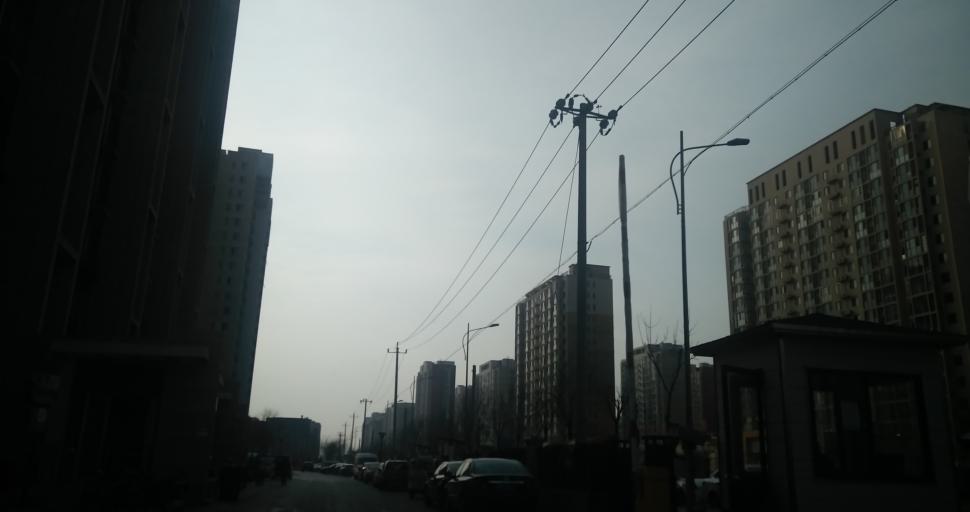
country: CN
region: Beijing
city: Yinghai
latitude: 39.7571
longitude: 116.4887
